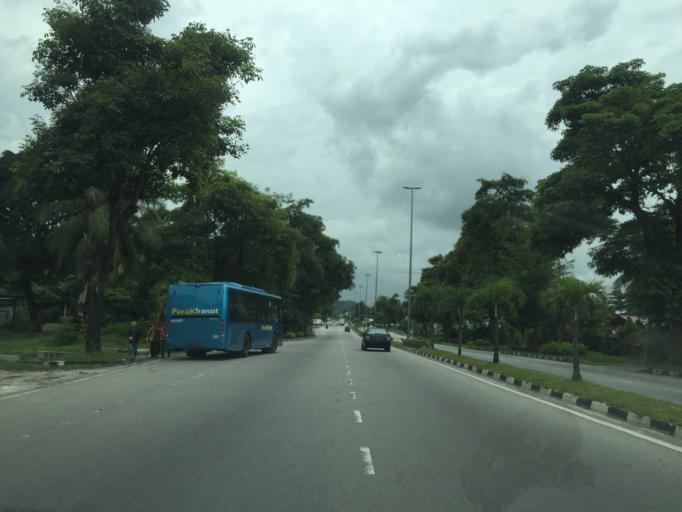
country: MY
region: Perak
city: Ipoh
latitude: 4.5423
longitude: 101.1217
